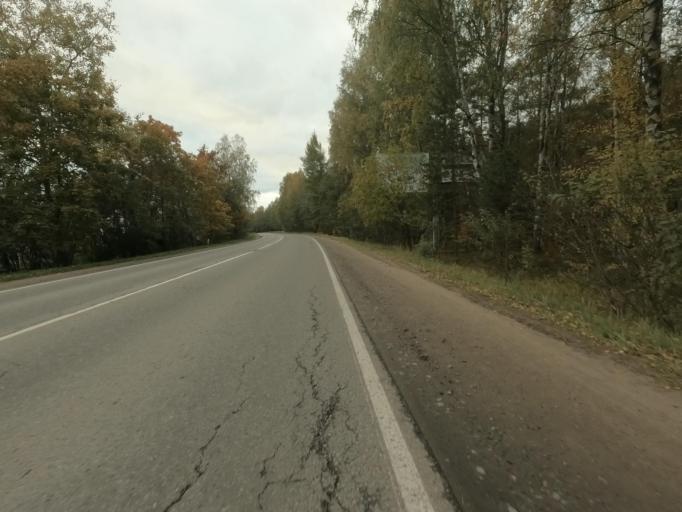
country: RU
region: Leningrad
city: Pavlovo
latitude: 59.7903
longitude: 30.9611
